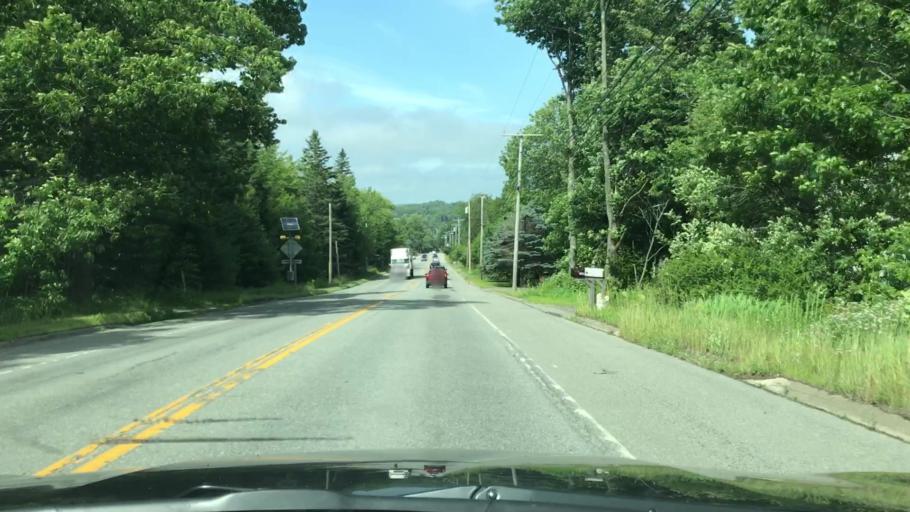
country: US
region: Maine
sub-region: Hancock County
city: Bucksport
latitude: 44.5608
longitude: -68.7924
